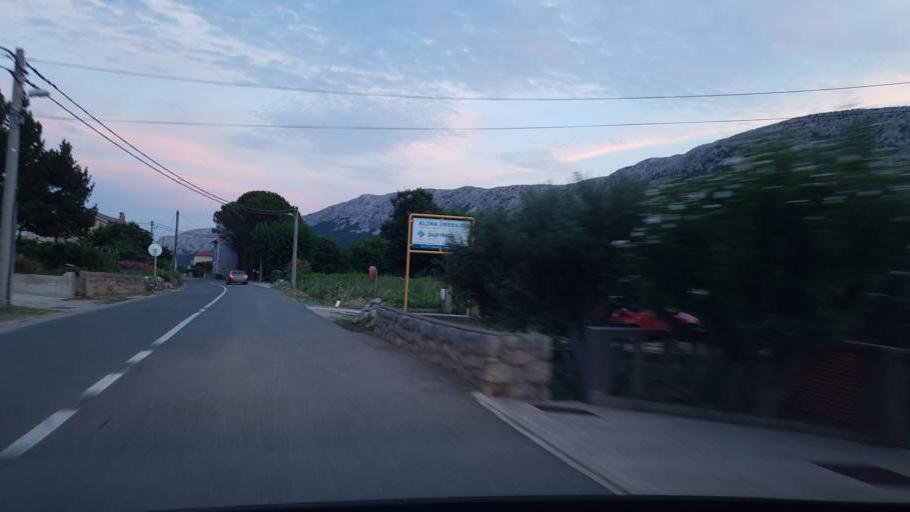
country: HR
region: Primorsko-Goranska
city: Punat
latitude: 44.9907
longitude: 14.7199
